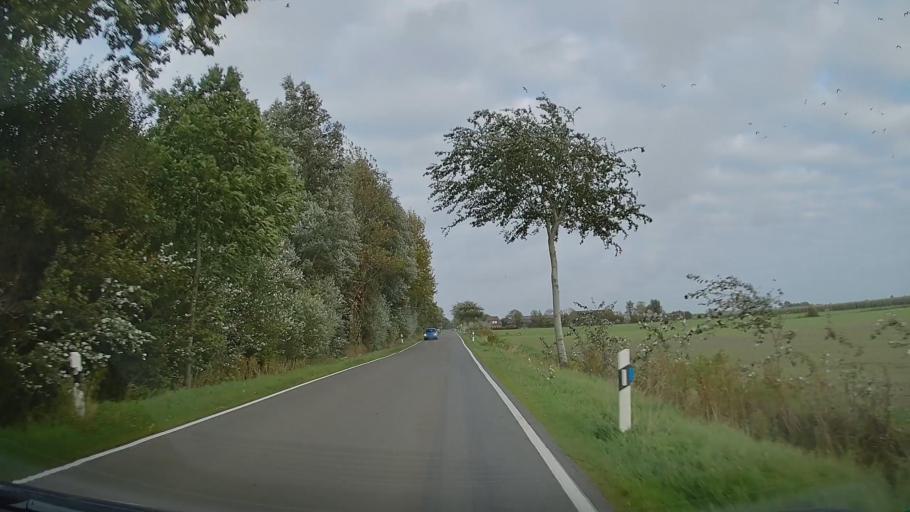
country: DE
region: Schleswig-Holstein
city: Osterhever
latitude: 54.4021
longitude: 8.7868
